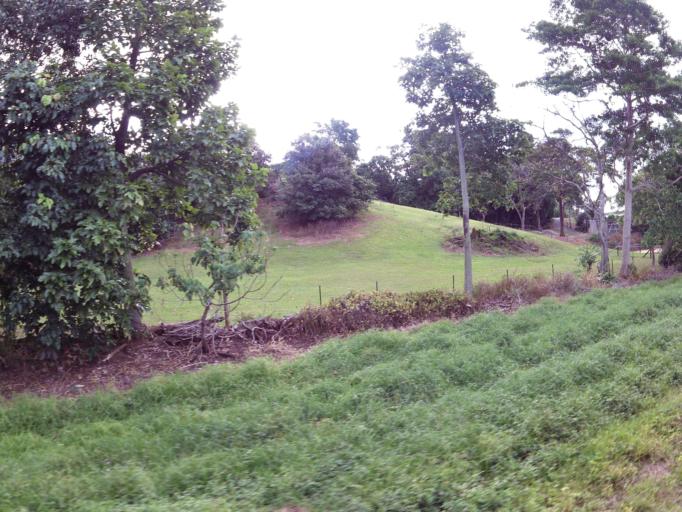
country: AU
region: Queensland
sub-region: Cairns
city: Redlynch
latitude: -16.8955
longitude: 145.6934
